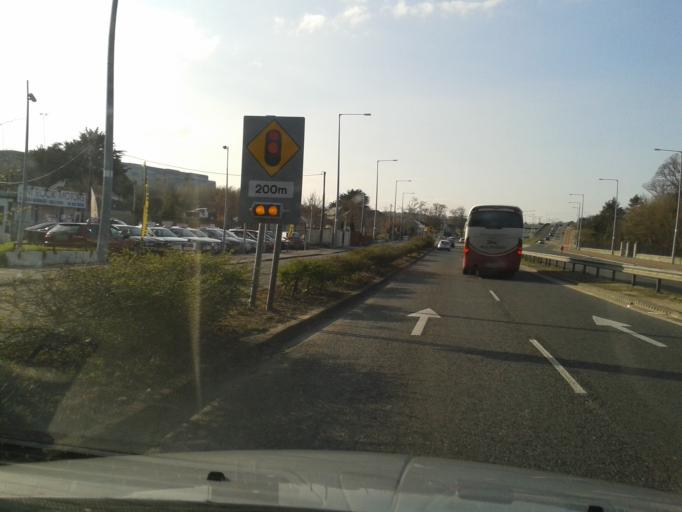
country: IE
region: Leinster
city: Loughlinstown
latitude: 53.2442
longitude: -6.1324
